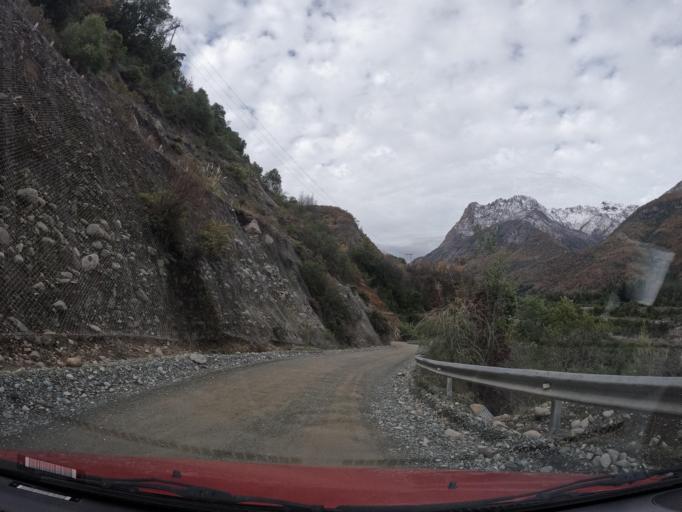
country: CL
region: Maule
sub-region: Provincia de Linares
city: Colbun
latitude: -35.8574
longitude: -71.2230
